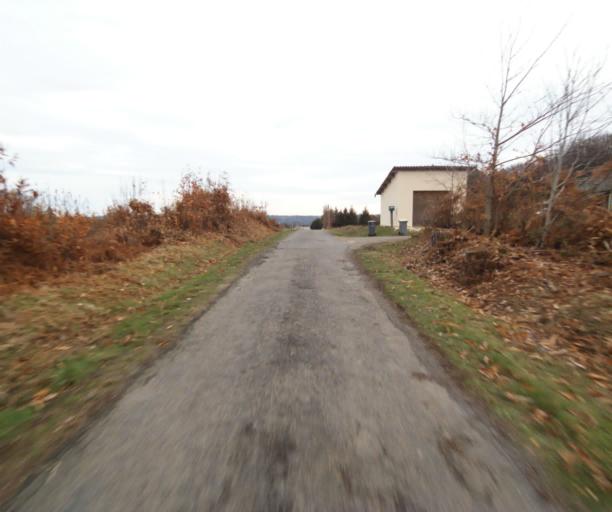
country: FR
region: Limousin
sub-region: Departement de la Correze
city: Chameyrat
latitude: 45.2349
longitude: 1.6617
